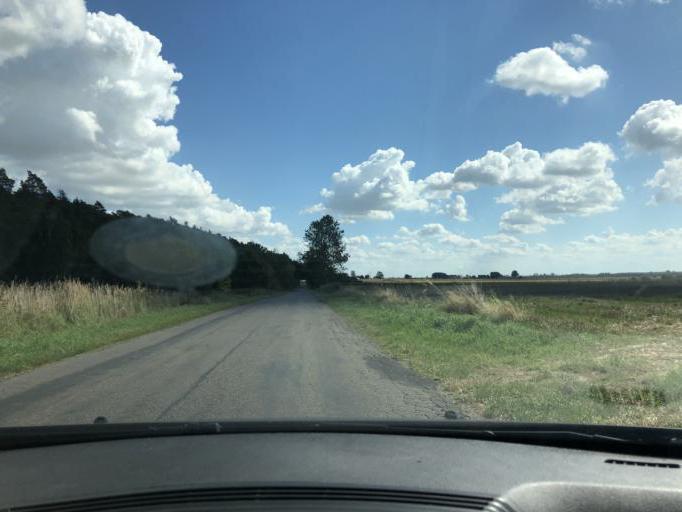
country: PL
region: Lodz Voivodeship
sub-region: Powiat wieruszowski
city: Czastary
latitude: 51.2603
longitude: 18.3480
